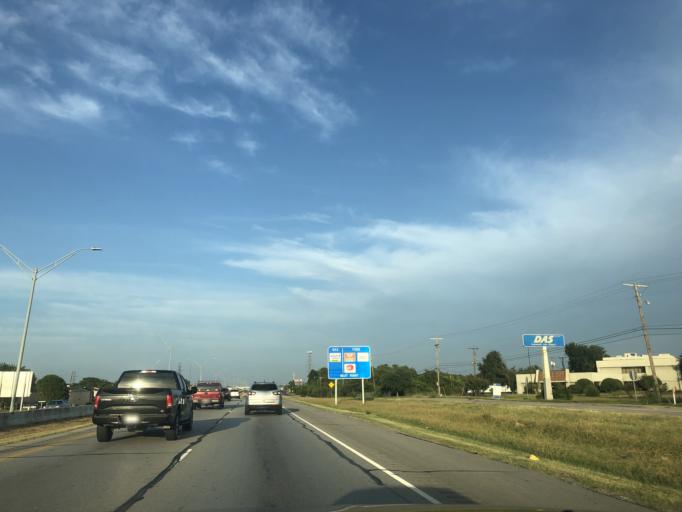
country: US
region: Texas
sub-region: Dallas County
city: Mesquite
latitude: 32.7923
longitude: -96.6454
